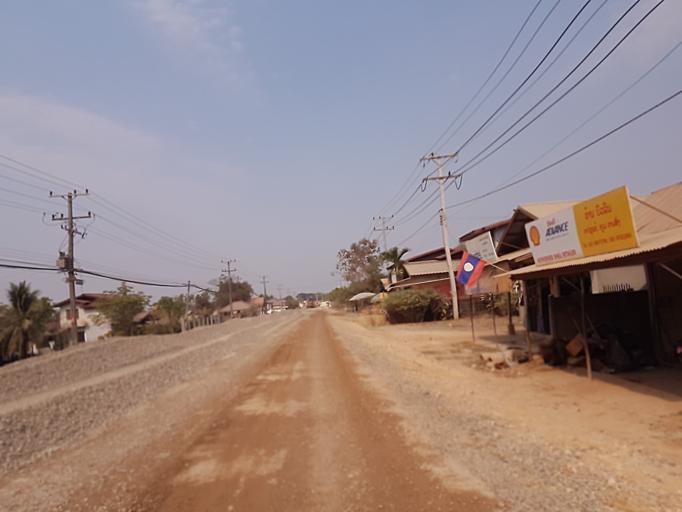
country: TH
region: Nong Khai
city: Nong Khai
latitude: 17.9054
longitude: 102.7601
